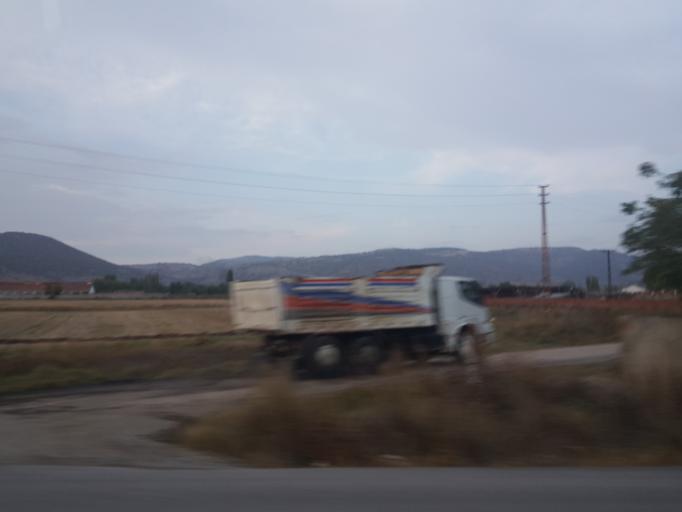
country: TR
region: Amasya
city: Gumushacikoy
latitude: 40.8775
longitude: 35.2310
